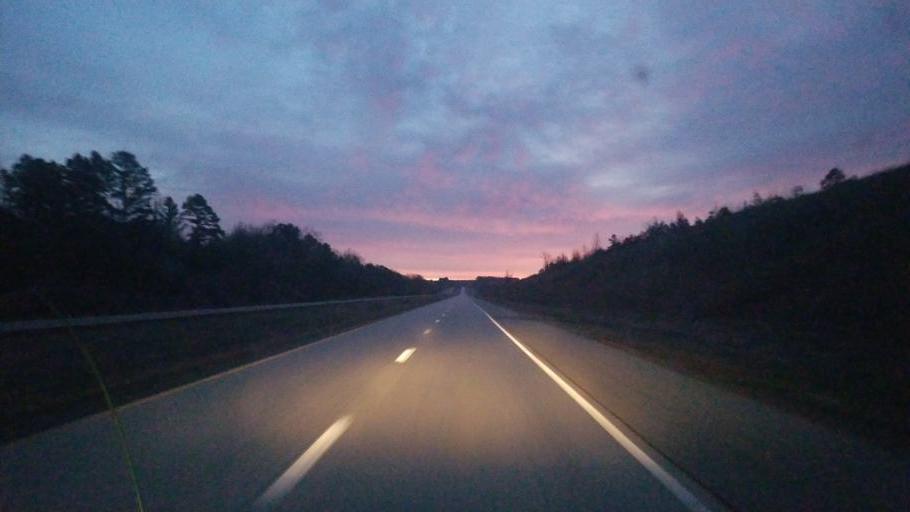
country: US
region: Missouri
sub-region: Shannon County
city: Winona
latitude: 36.9972
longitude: -91.4471
